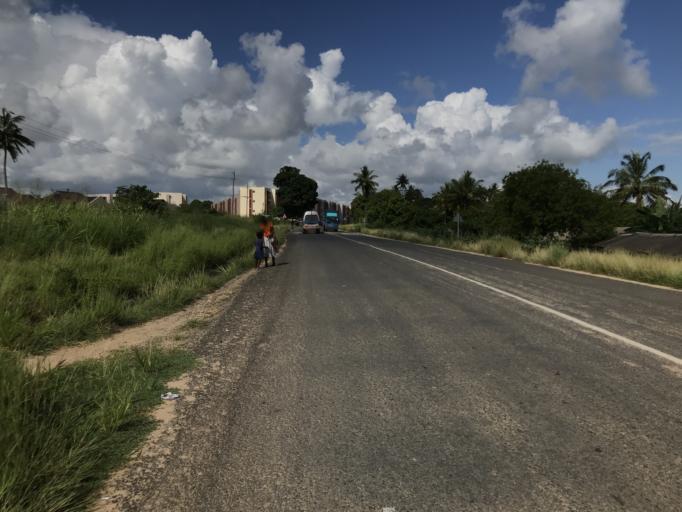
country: TZ
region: Dar es Salaam
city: Dar es Salaam
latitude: -6.8889
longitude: 39.4260
